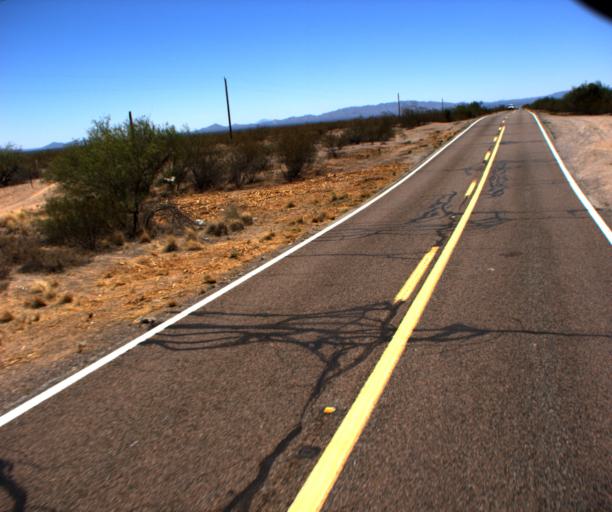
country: US
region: Arizona
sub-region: Pima County
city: Ajo
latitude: 32.2028
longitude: -112.5163
